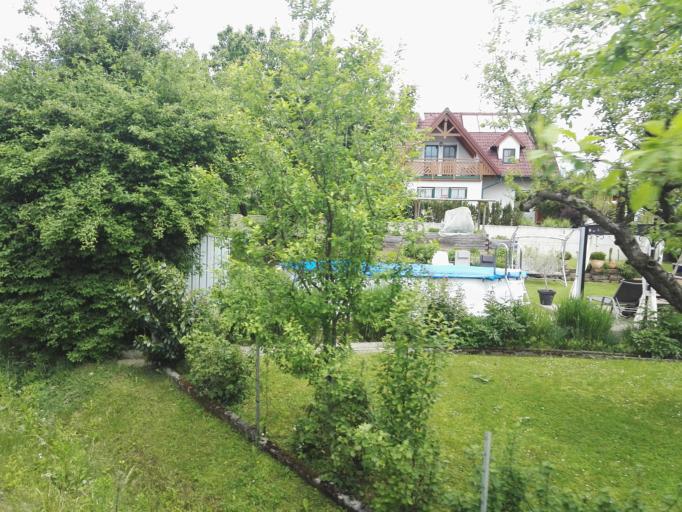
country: AT
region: Styria
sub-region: Politischer Bezirk Weiz
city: Krottendorf
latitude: 47.2126
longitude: 15.6397
